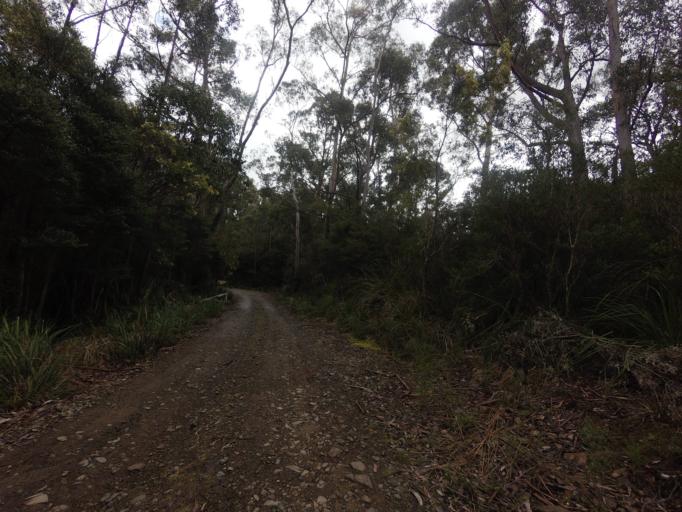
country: AU
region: Tasmania
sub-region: Huon Valley
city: Geeveston
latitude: -43.4558
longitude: 146.9042
